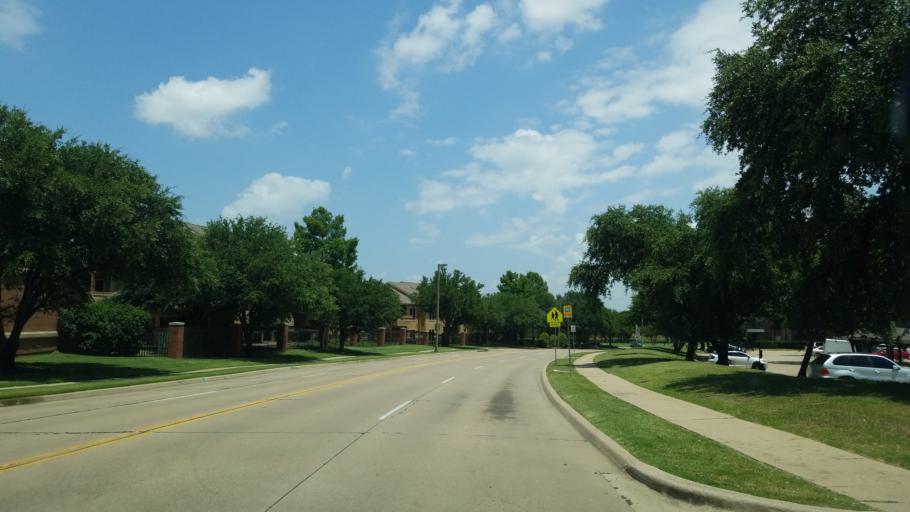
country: US
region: Texas
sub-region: Dallas County
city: Coppell
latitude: 32.9449
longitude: -96.9554
